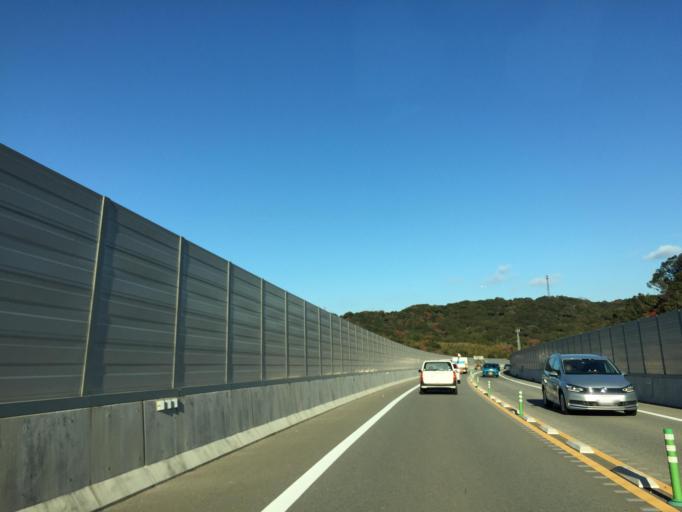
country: JP
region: Wakayama
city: Wakayama-shi
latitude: 34.2884
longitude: 135.1527
